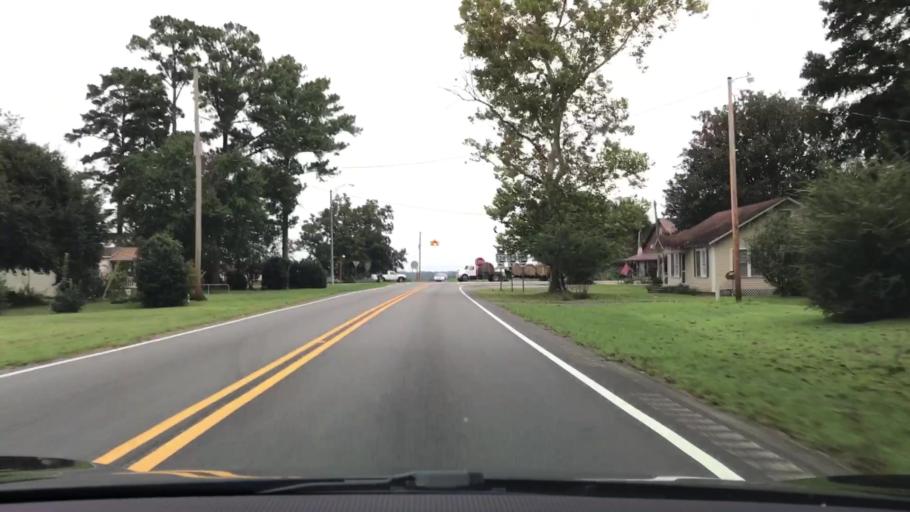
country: US
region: Alabama
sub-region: Covington County
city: Opp
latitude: 31.2794
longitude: -86.1574
